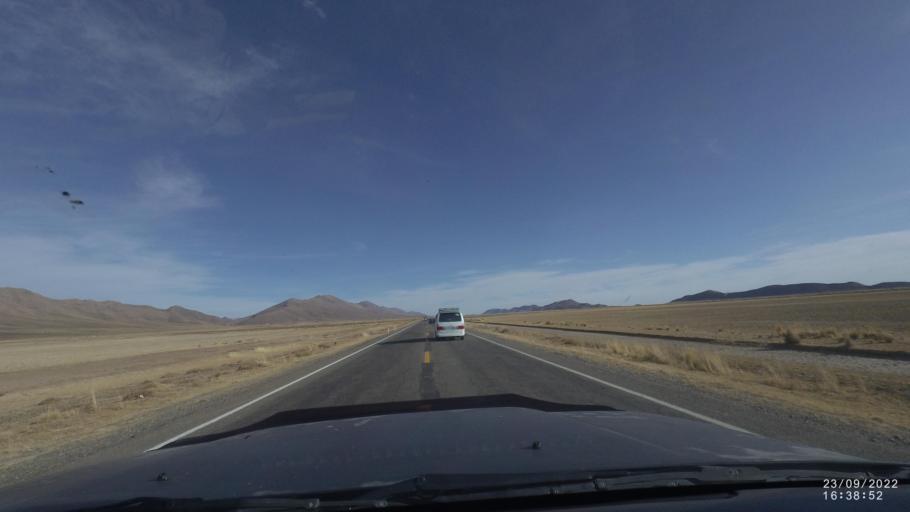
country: BO
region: Oruro
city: Machacamarca
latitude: -18.2531
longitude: -67.0010
